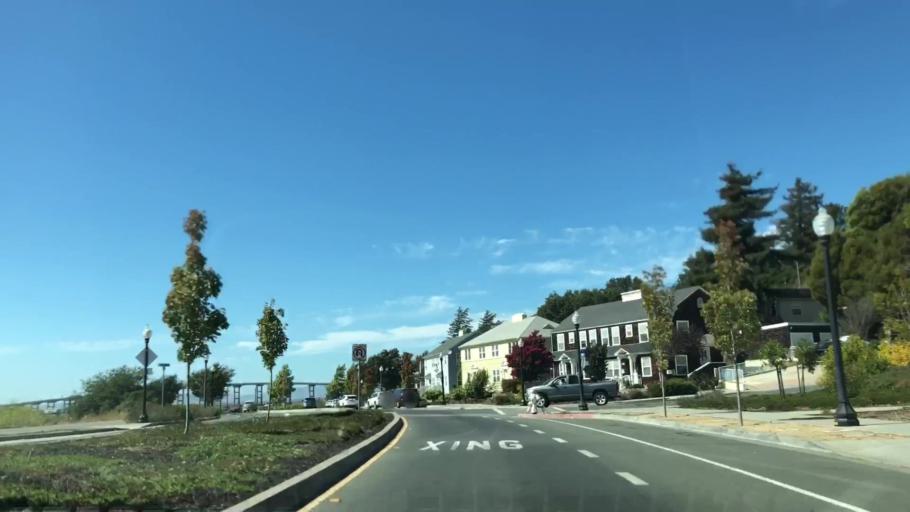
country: US
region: California
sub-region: Solano County
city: Vallejo
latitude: 38.1140
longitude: -122.2675
